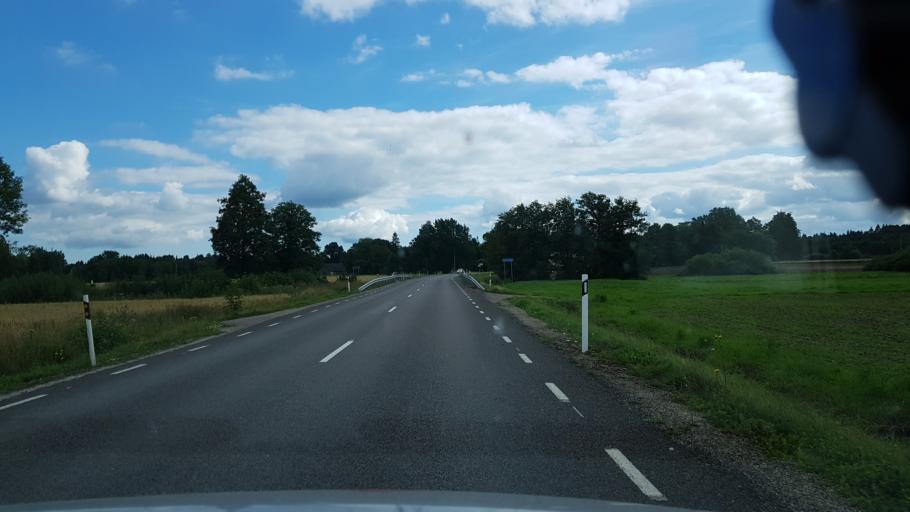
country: EE
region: Ida-Virumaa
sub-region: Kivioli linn
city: Kivioli
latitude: 59.1210
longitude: 26.9221
